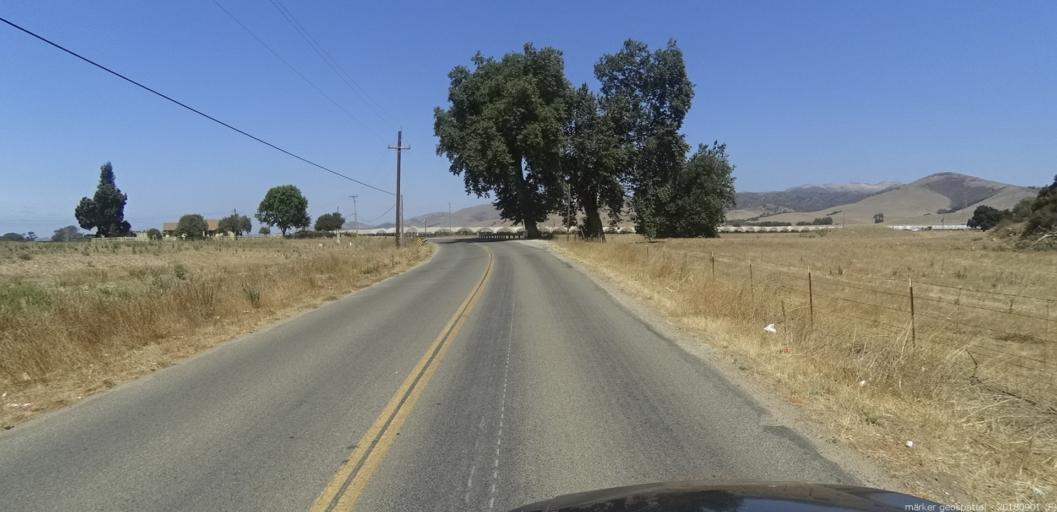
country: US
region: California
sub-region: Monterey County
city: Salinas
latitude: 36.6916
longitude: -121.5690
